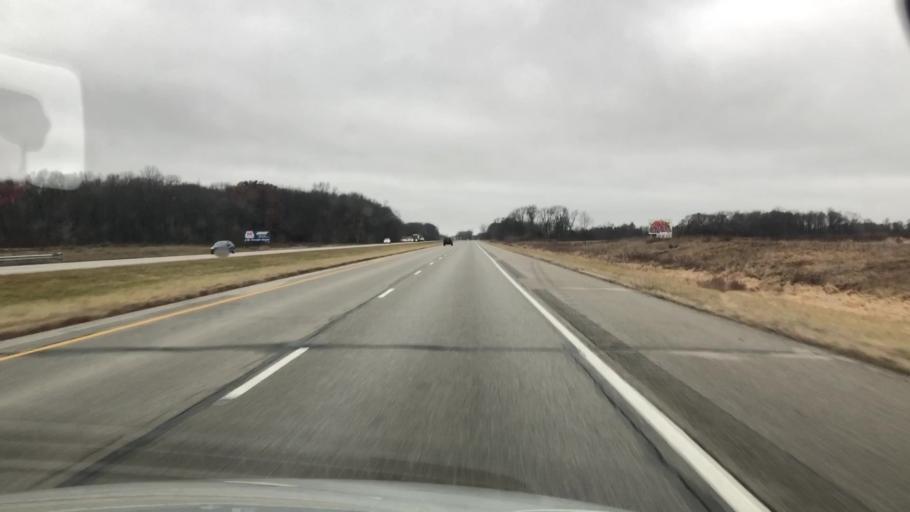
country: US
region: Indiana
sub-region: Kosciusko County
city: Mentone
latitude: 41.2684
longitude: -86.0017
